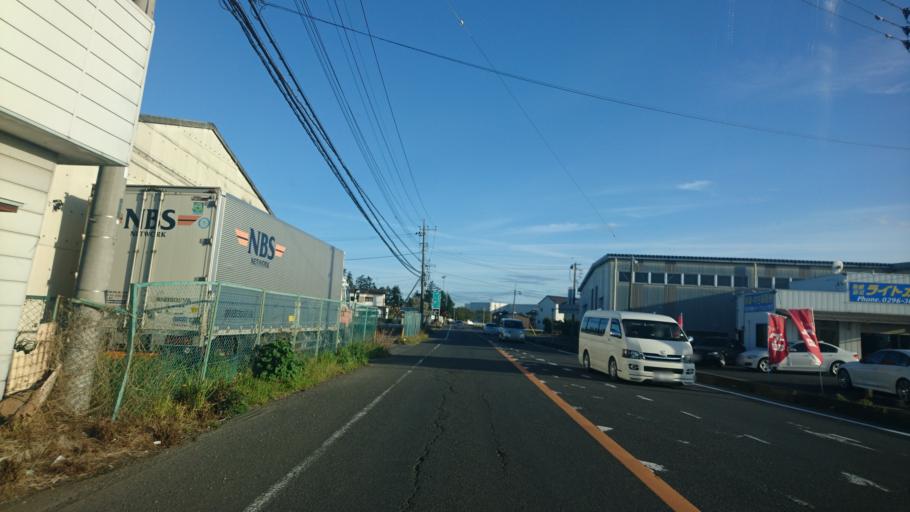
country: JP
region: Ibaraki
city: Ishige
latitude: 36.1977
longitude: 139.9565
